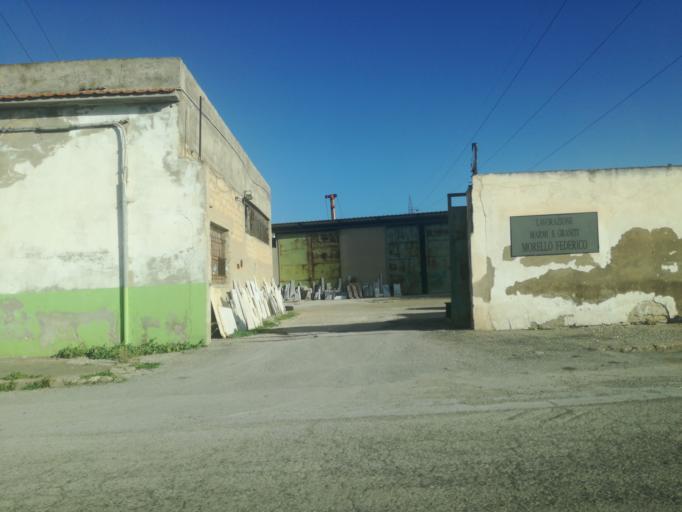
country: IT
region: Sicily
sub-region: Provincia di Caltanissetta
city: Gela
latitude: 37.0621
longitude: 14.2718
